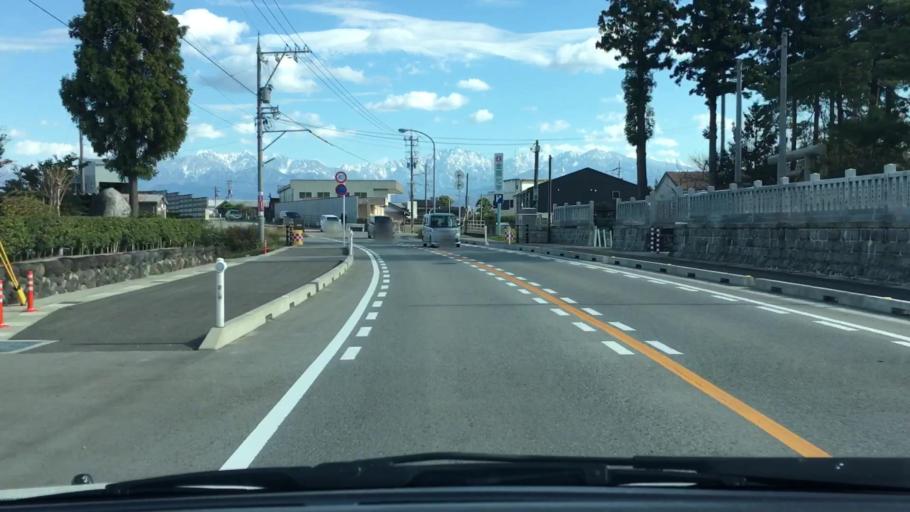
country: JP
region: Toyama
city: Toyama-shi
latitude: 36.7024
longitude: 137.2686
